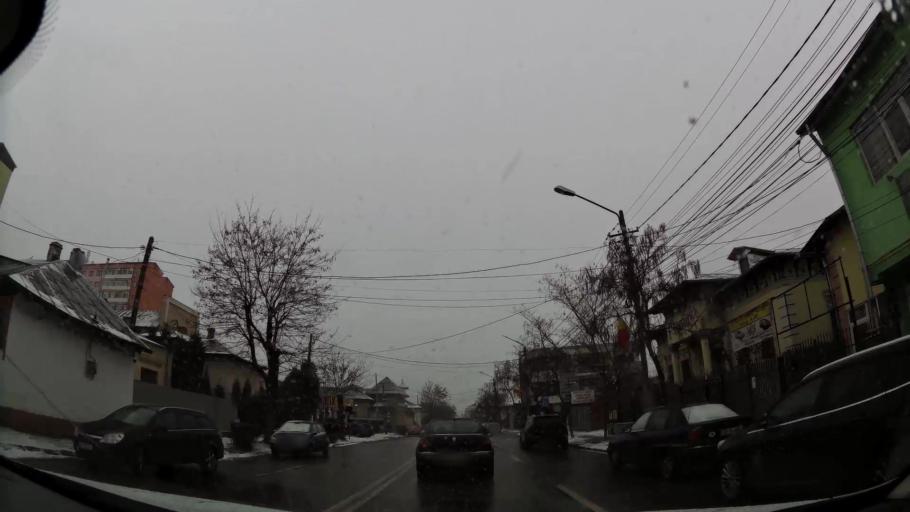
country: RO
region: Dambovita
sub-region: Municipiul Targoviste
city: Targoviste
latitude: 44.9215
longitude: 25.4751
